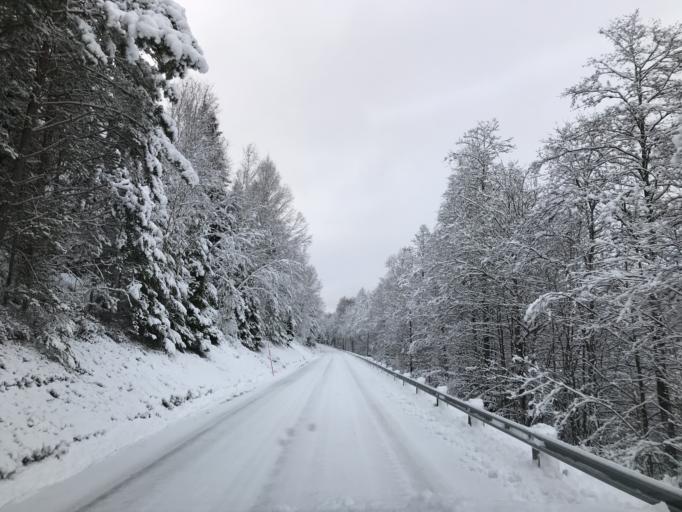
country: SE
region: Vaestra Goetaland
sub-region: Bollebygds Kommun
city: Bollebygd
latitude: 57.7975
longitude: 12.6563
